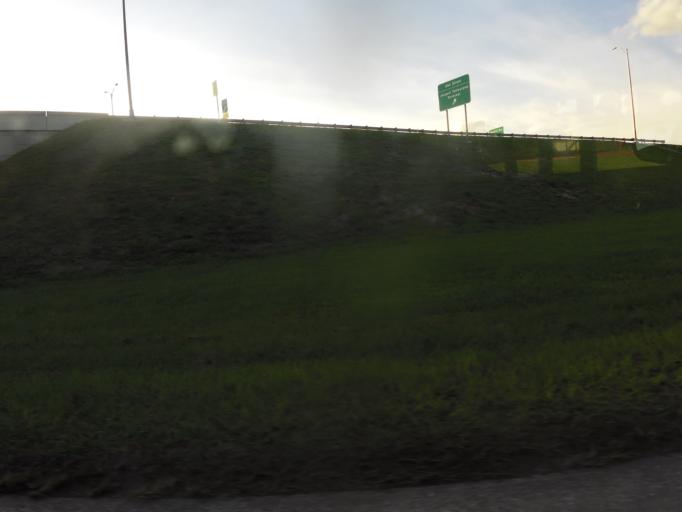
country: US
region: Florida
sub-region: Duval County
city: Jacksonville
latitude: 30.3554
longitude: -81.6369
